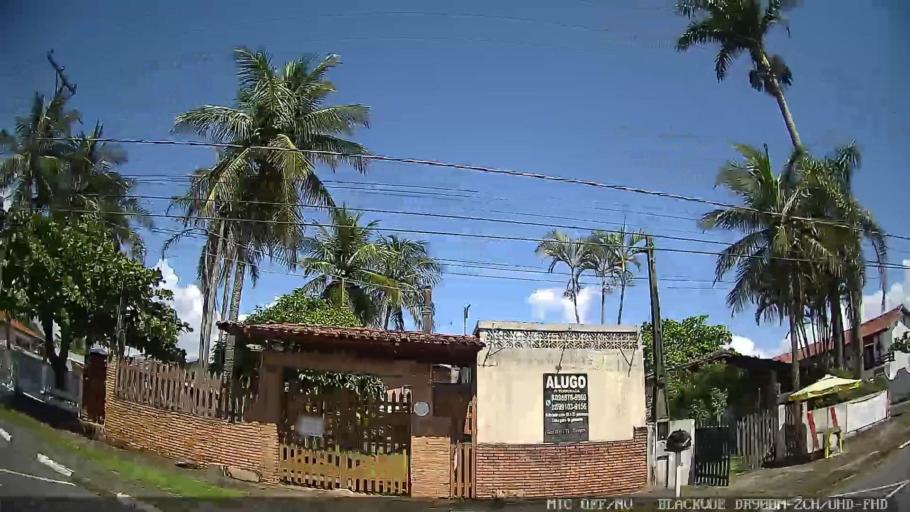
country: BR
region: Sao Paulo
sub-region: Caraguatatuba
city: Caraguatatuba
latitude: -23.6837
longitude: -45.4320
